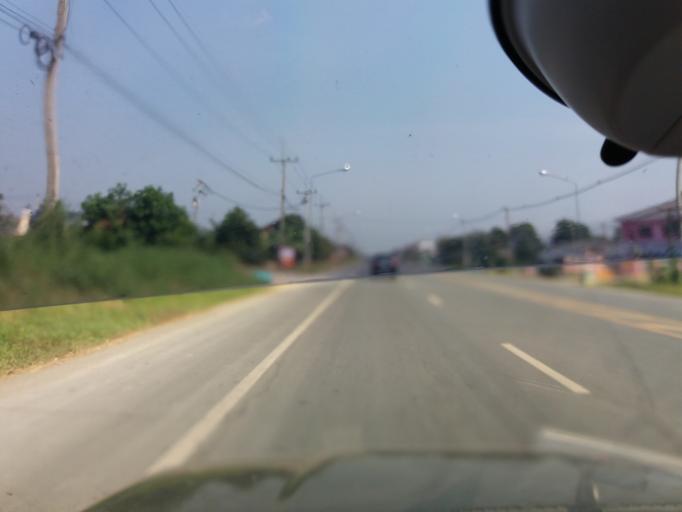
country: TH
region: Sing Buri
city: Bang Racham
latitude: 14.8826
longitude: 100.3301
